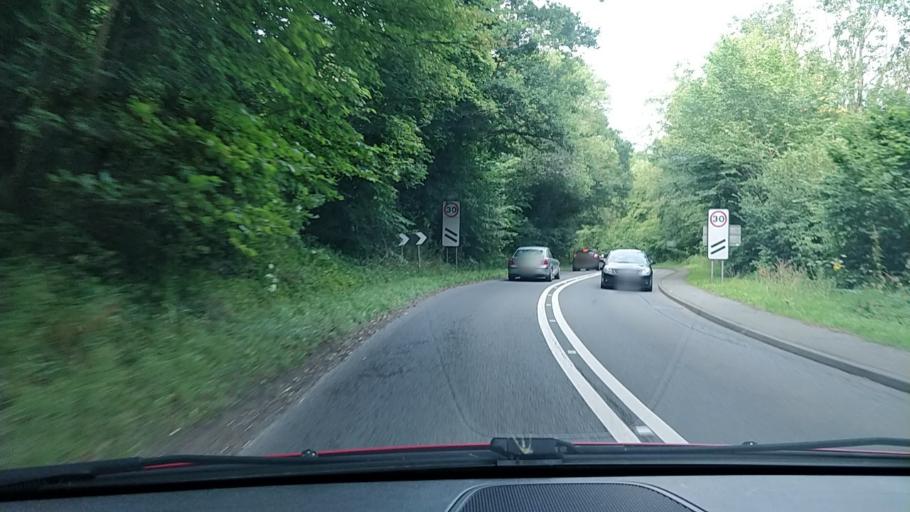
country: GB
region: Wales
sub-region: County of Flintshire
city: Leeswood
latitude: 53.1177
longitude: -3.0996
